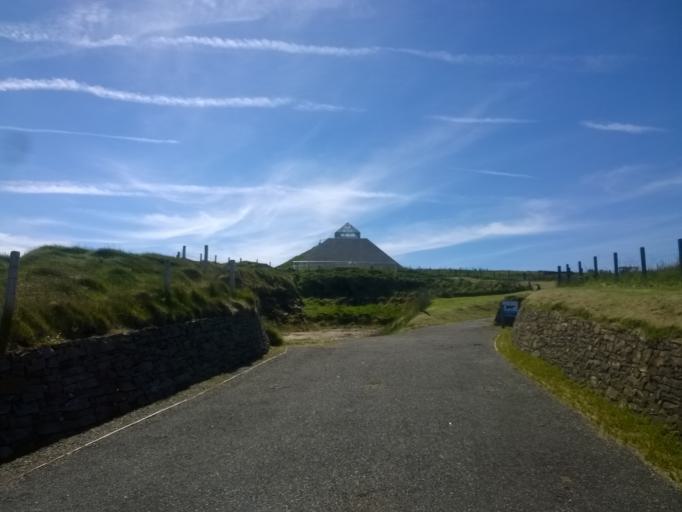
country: IE
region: Connaught
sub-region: Maigh Eo
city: Crossmolina
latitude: 54.3081
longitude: -9.4566
